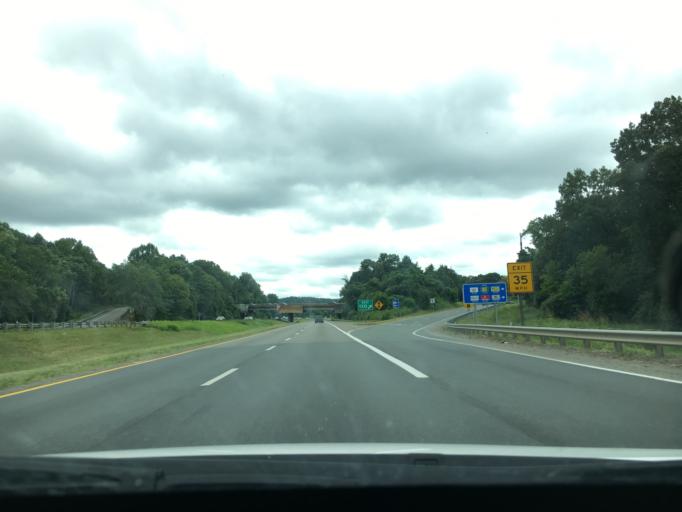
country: US
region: Virginia
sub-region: City of Charlottesville
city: Charlottesville
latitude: 38.0081
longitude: -78.5049
